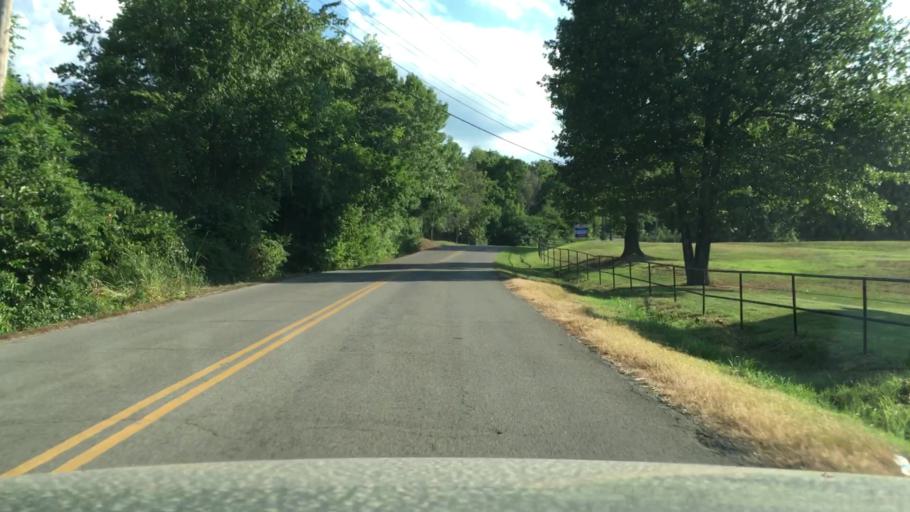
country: US
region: Oklahoma
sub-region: Muskogee County
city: Fort Gibson
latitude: 35.9175
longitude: -95.1545
